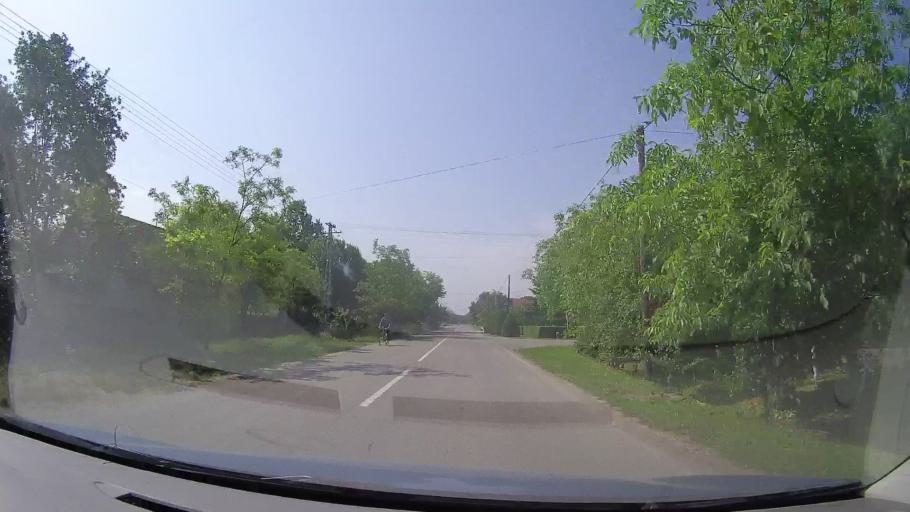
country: RS
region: Autonomna Pokrajina Vojvodina
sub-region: Srednjebanatski Okrug
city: Secanj
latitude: 45.3725
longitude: 20.7777
